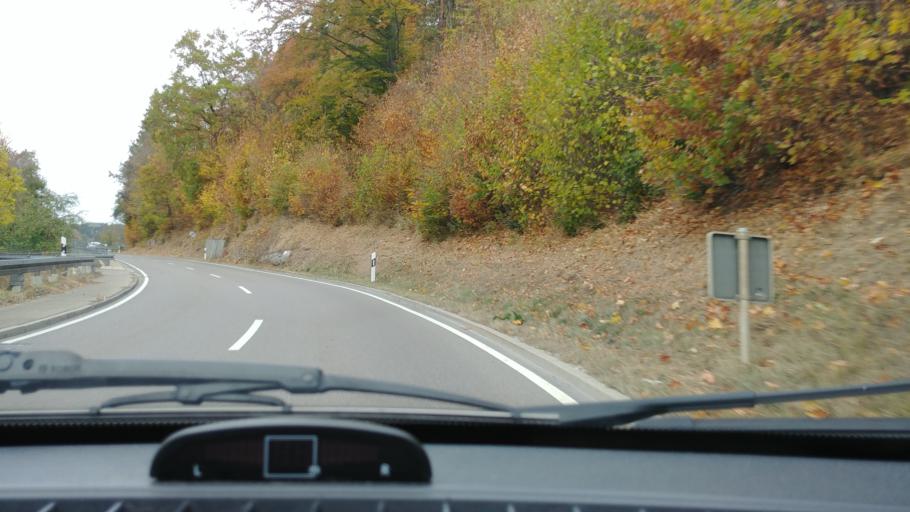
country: DE
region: Baden-Wuerttemberg
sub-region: Regierungsbezirk Stuttgart
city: Jagstzell
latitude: 49.0164
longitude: 10.1079
